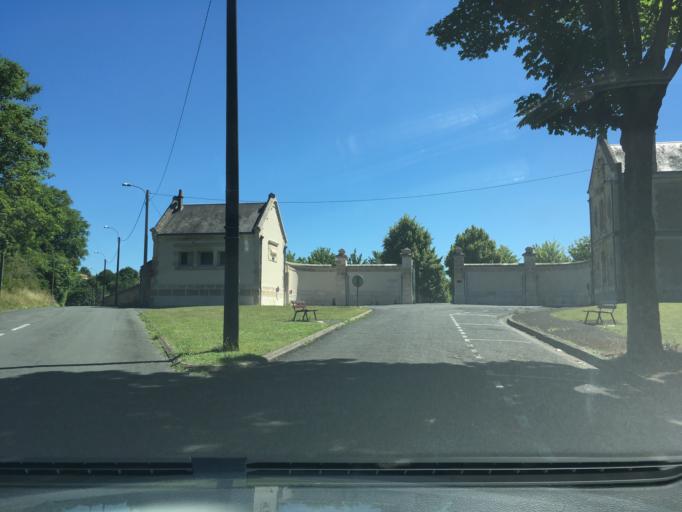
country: FR
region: Poitou-Charentes
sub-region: Departement des Deux-Sevres
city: Niort
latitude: 46.3241
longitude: -0.4470
